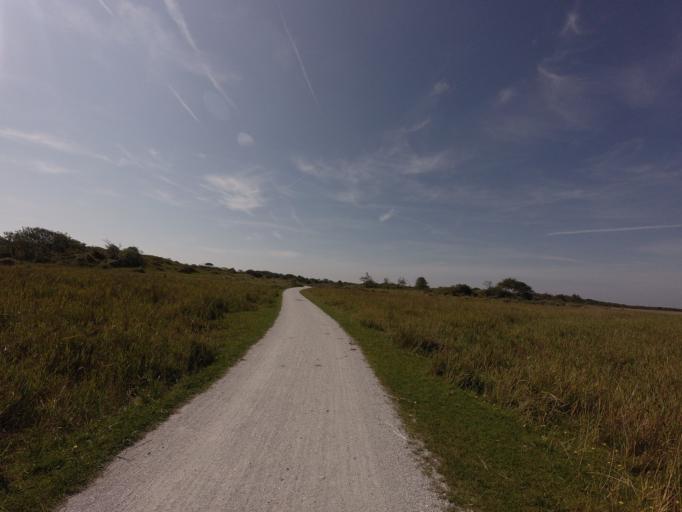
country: NL
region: Friesland
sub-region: Gemeente Schiermonnikoog
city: Schiermonnikoog
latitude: 53.4854
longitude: 6.2050
